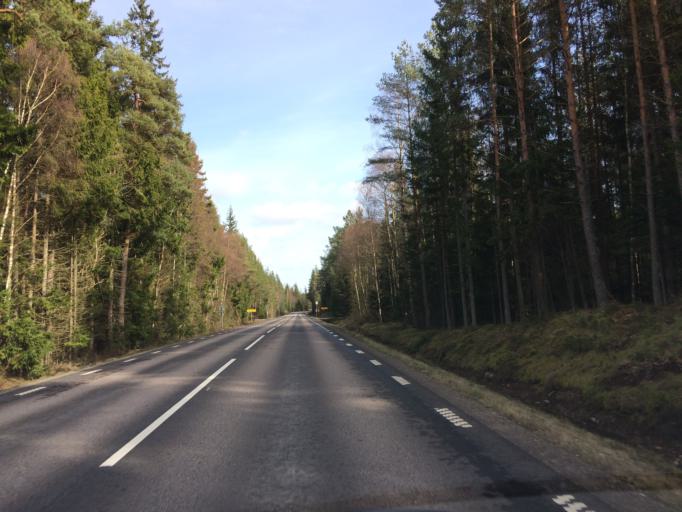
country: SE
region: Halland
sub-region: Hylte Kommun
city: Hyltebruk
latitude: 57.0211
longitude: 13.1852
